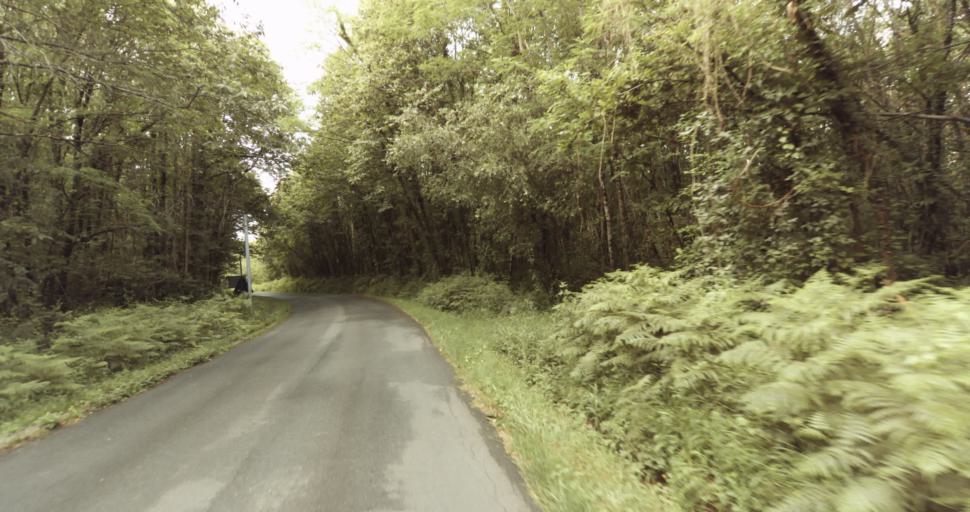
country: FR
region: Aquitaine
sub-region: Departement de la Dordogne
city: Le Bugue
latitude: 44.9356
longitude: 0.8186
